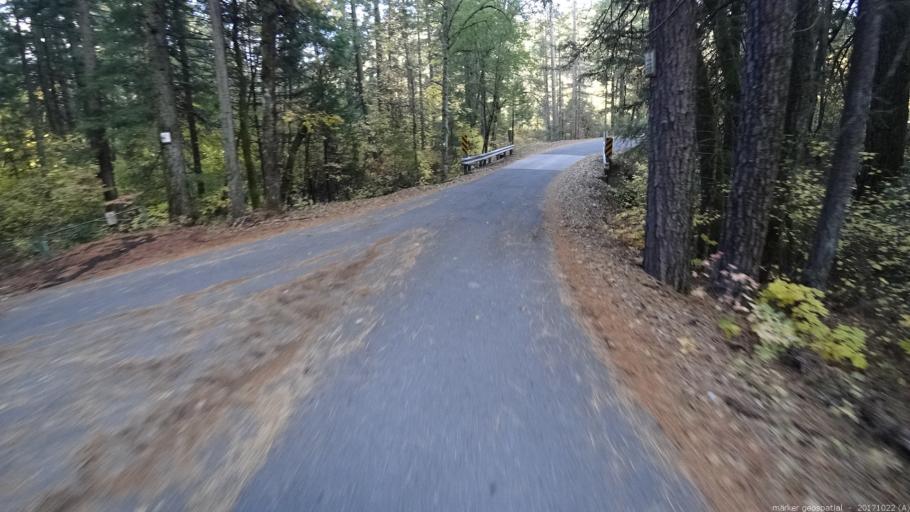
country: US
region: California
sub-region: Siskiyou County
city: Dunsmuir
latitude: 41.1604
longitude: -122.2921
